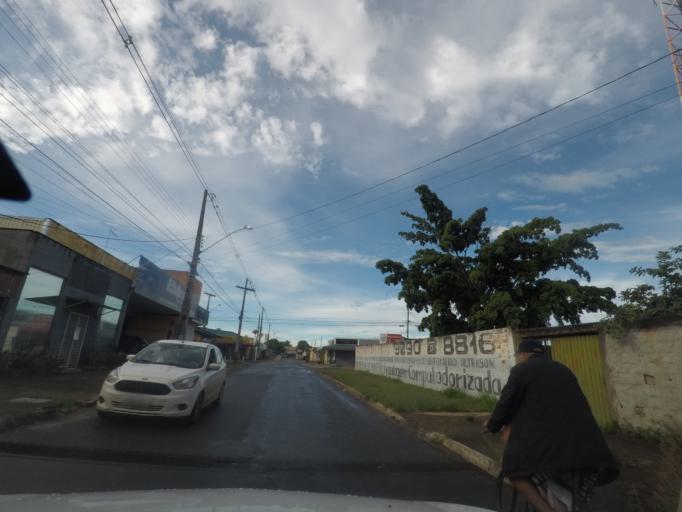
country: BR
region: Goias
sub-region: Aparecida De Goiania
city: Aparecida de Goiania
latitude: -16.7657
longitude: -49.3519
